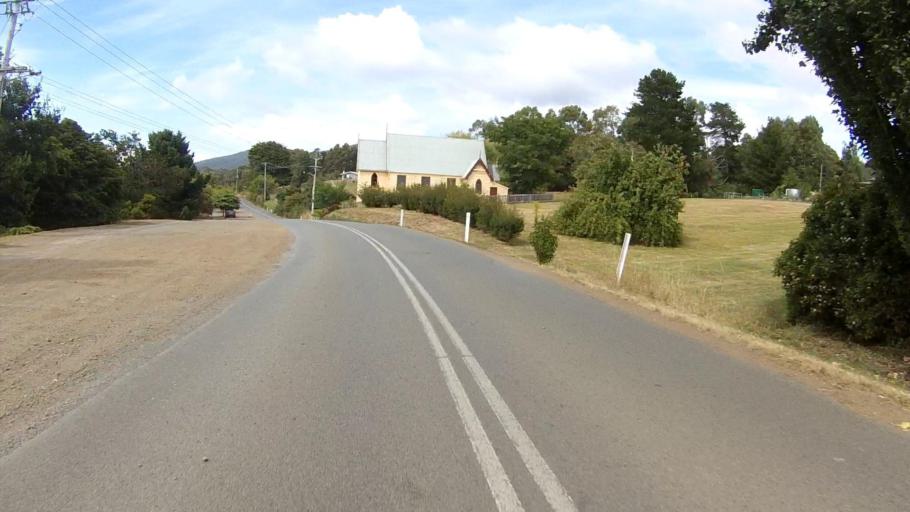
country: AU
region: Tasmania
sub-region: Kingborough
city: Kettering
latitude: -43.1608
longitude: 147.2383
